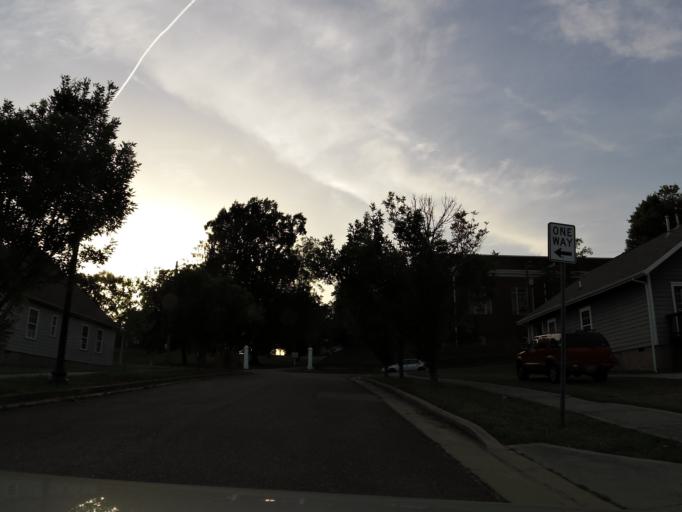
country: US
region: Tennessee
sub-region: Knox County
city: Knoxville
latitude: 35.9692
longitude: -83.9406
